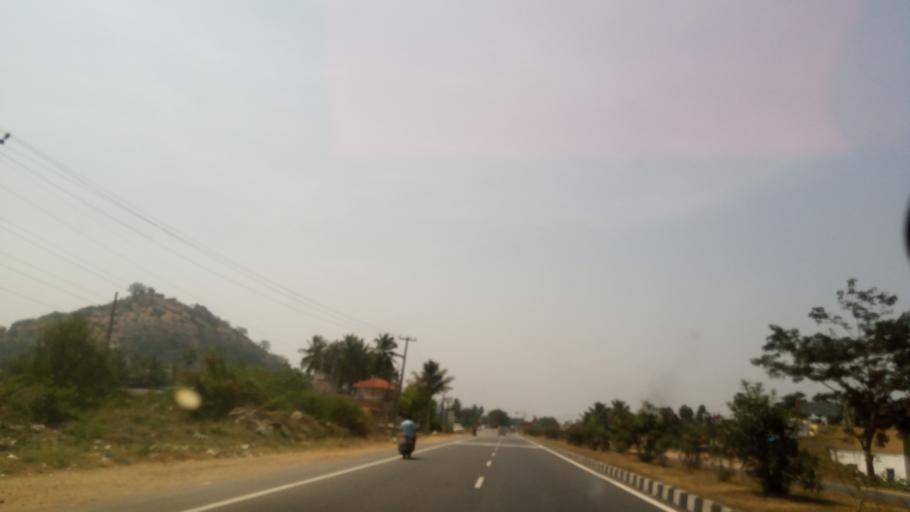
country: IN
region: Tamil Nadu
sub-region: Salem
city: Salem
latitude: 11.6502
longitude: 78.1895
